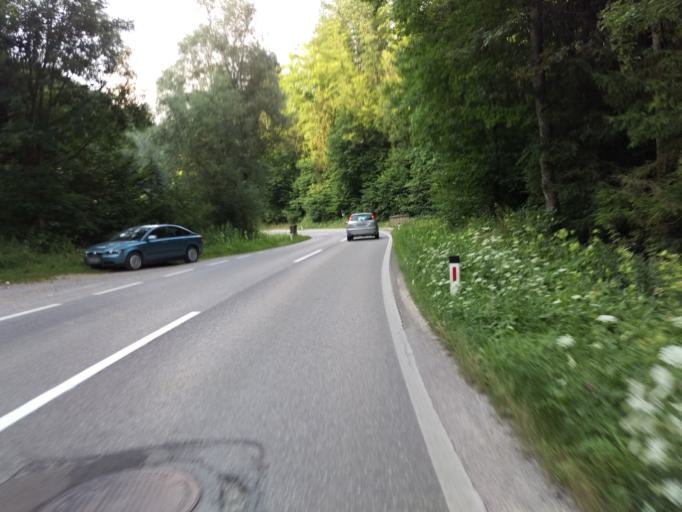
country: AT
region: Styria
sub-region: Politischer Bezirk Graz-Umgebung
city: Thal
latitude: 47.0766
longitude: 15.3646
